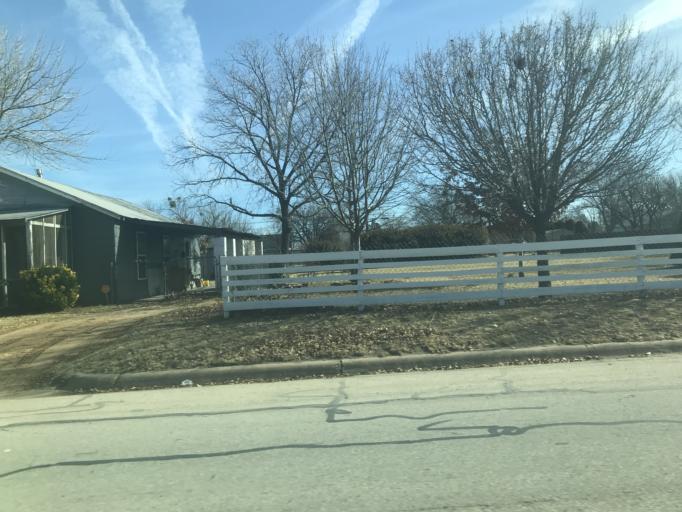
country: US
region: Texas
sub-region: Taylor County
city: Abilene
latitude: 32.4847
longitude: -99.7394
